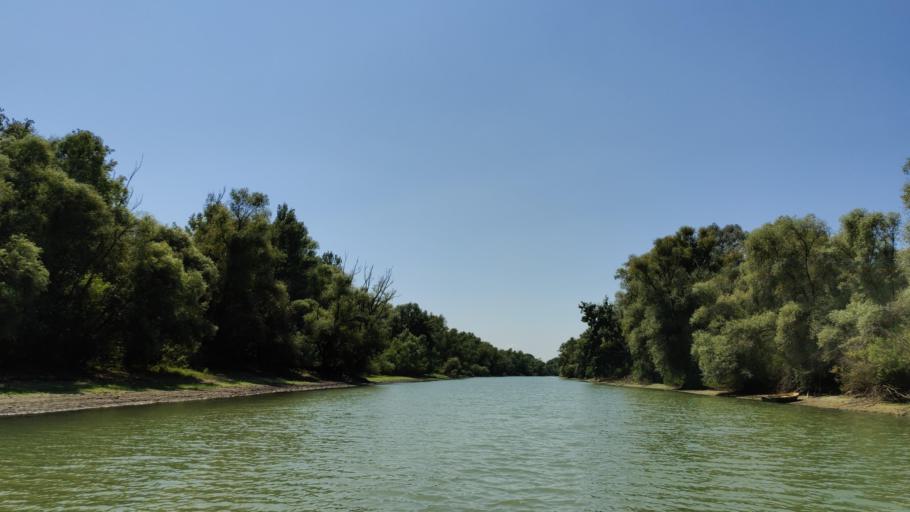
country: RO
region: Tulcea
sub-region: Comuna Nufaru
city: Nufaru
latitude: 45.2248
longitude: 28.8858
